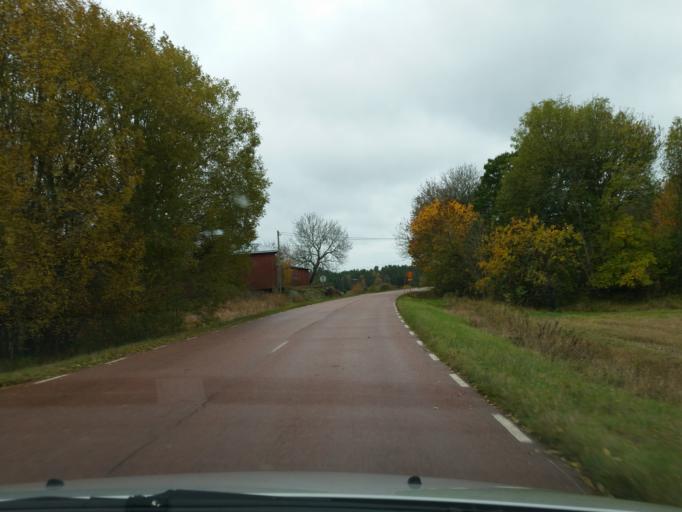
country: AX
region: Alands landsbygd
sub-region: Lumparland
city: Lumparland
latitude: 60.1171
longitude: 20.2646
